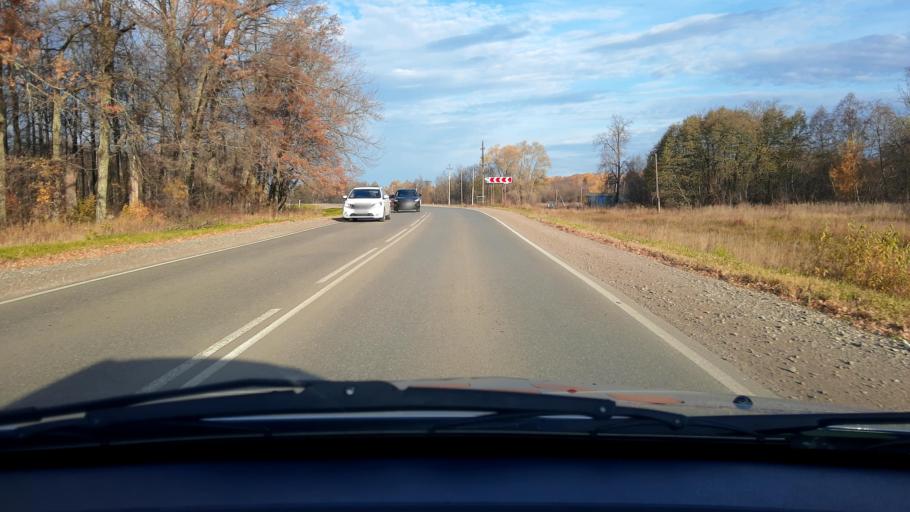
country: RU
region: Bashkortostan
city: Mikhaylovka
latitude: 54.8059
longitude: 55.8228
